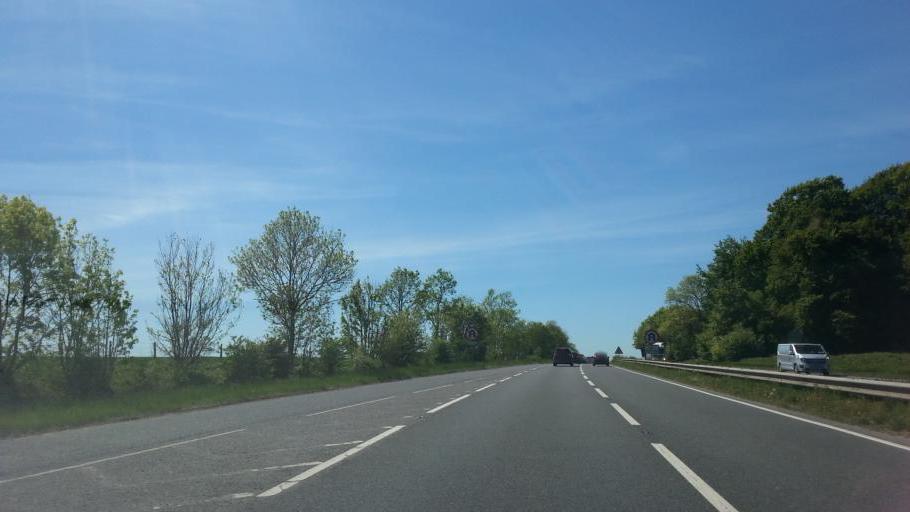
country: GB
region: England
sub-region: Wiltshire
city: Amesbury
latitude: 51.1769
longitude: -1.8059
